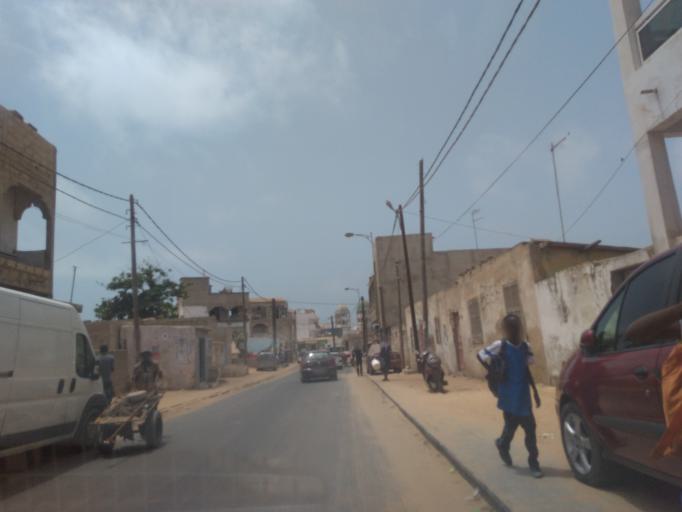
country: SN
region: Dakar
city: Pikine
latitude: 14.7678
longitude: -17.4299
